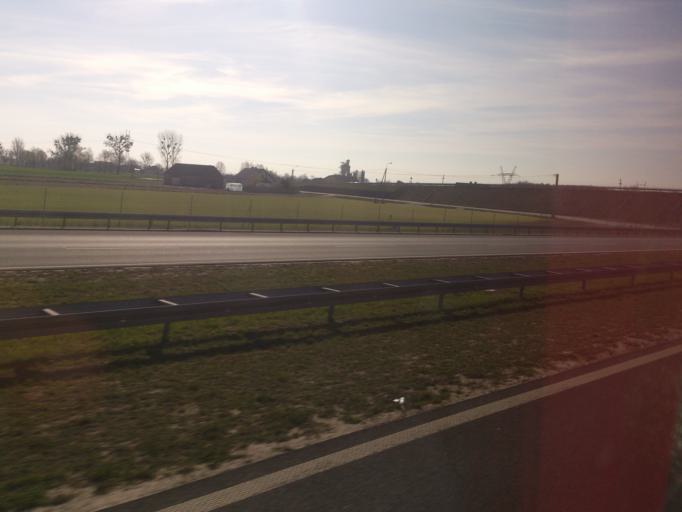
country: PL
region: Kujawsko-Pomorskie
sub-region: Powiat aleksandrowski
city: Waganiec
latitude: 52.7869
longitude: 18.8419
